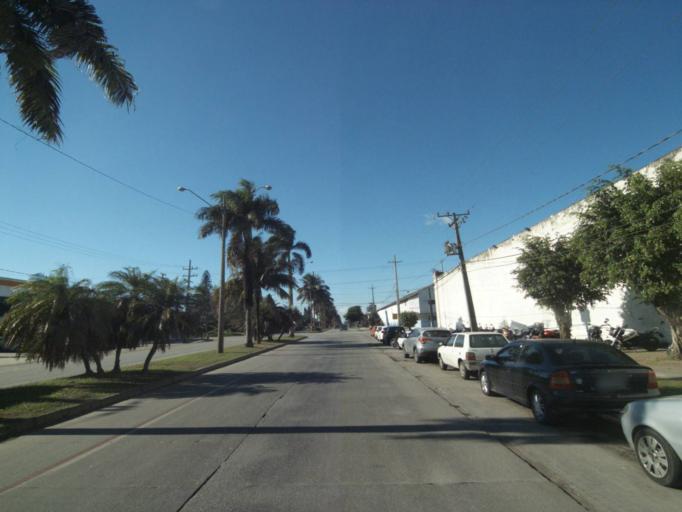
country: BR
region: Parana
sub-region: Paranagua
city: Paranagua
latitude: -25.5099
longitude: -48.5110
